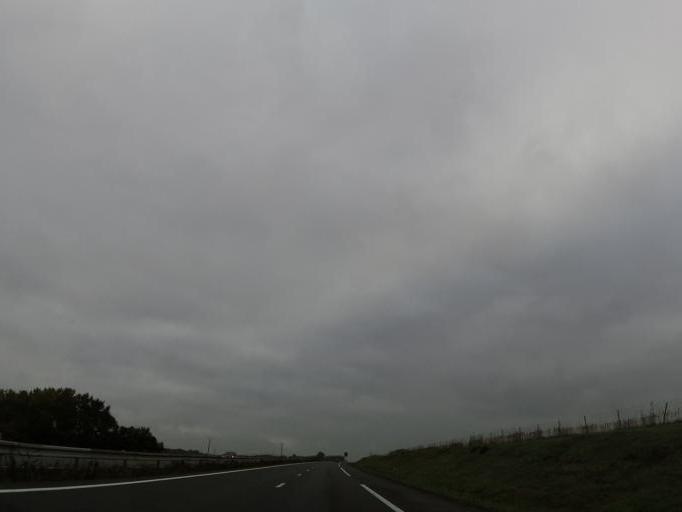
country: FR
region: Ile-de-France
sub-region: Departement de Seine-et-Marne
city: La Ferte-sous-Jouarre
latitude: 48.9945
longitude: 3.1092
